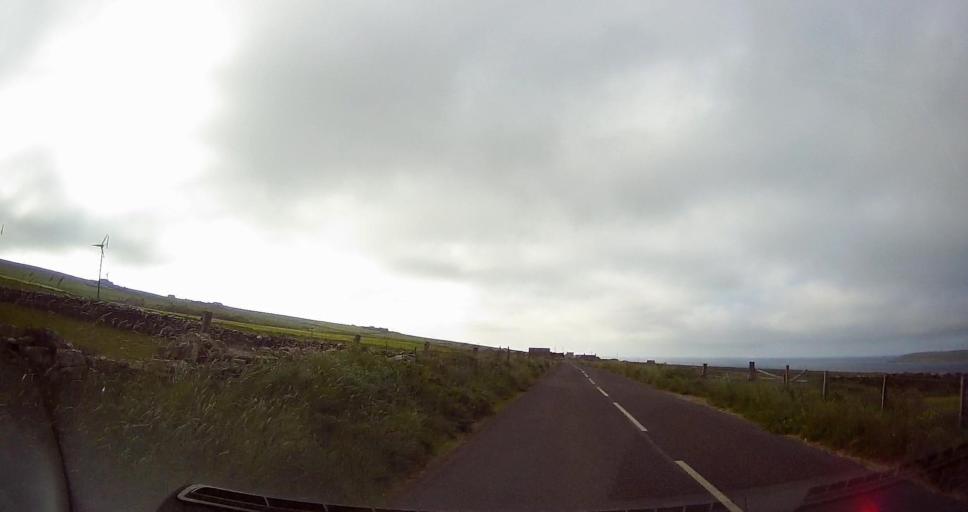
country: GB
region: Scotland
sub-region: Orkney Islands
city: Orkney
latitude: 59.1196
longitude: -3.1211
